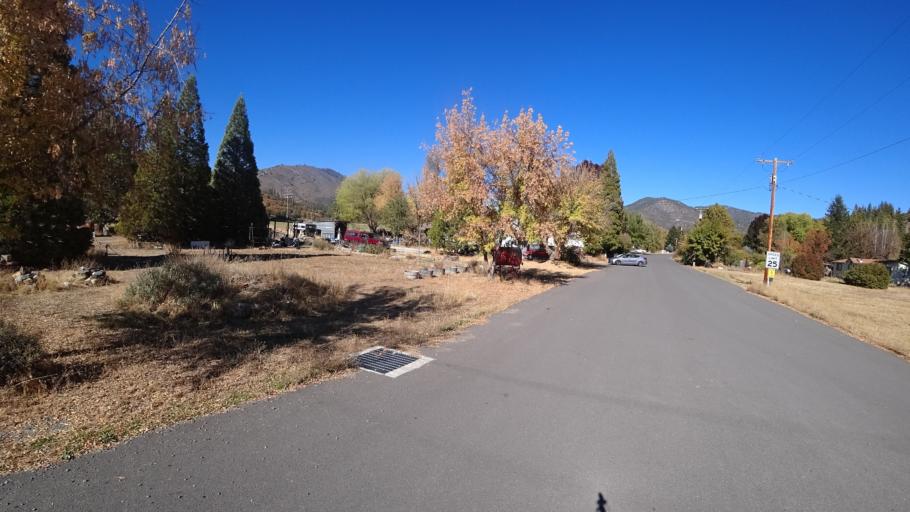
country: US
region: California
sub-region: Siskiyou County
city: Yreka
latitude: 41.6155
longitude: -122.8375
